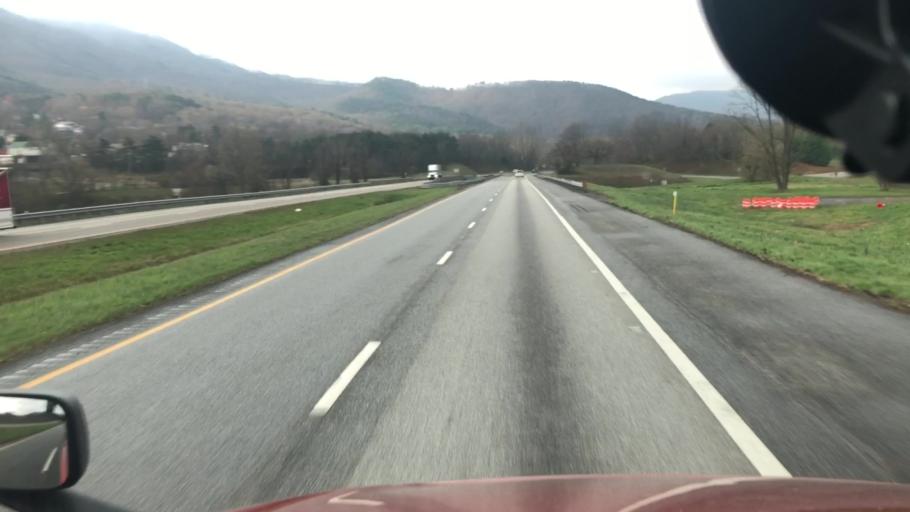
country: US
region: Virginia
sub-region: Alleghany County
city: Clifton Forge
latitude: 37.8110
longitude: -79.8483
